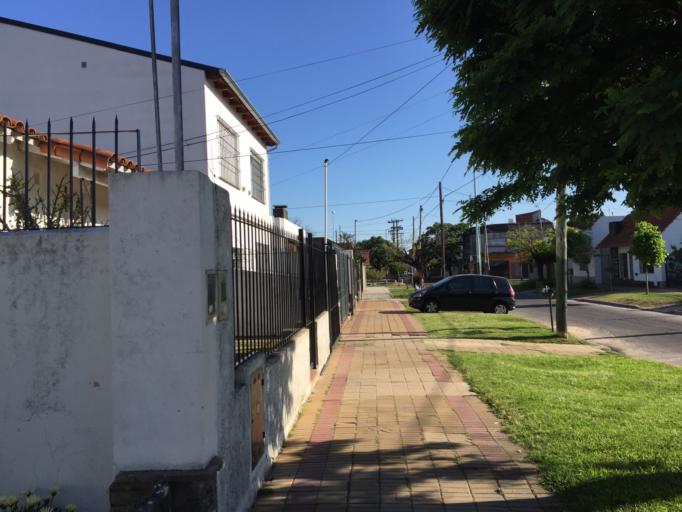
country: AR
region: Buenos Aires
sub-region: Partido de Lomas de Zamora
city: Lomas de Zamora
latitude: -34.7376
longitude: -58.3876
